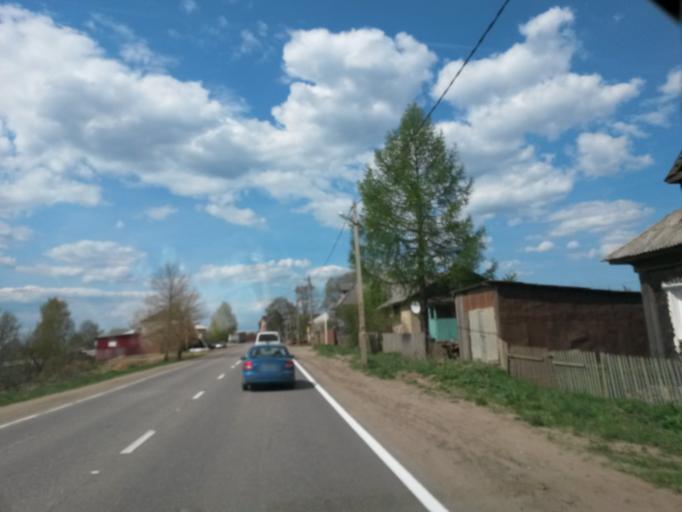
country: RU
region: Jaroslavl
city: Bol'shoye Selo
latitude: 57.7239
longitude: 38.9345
